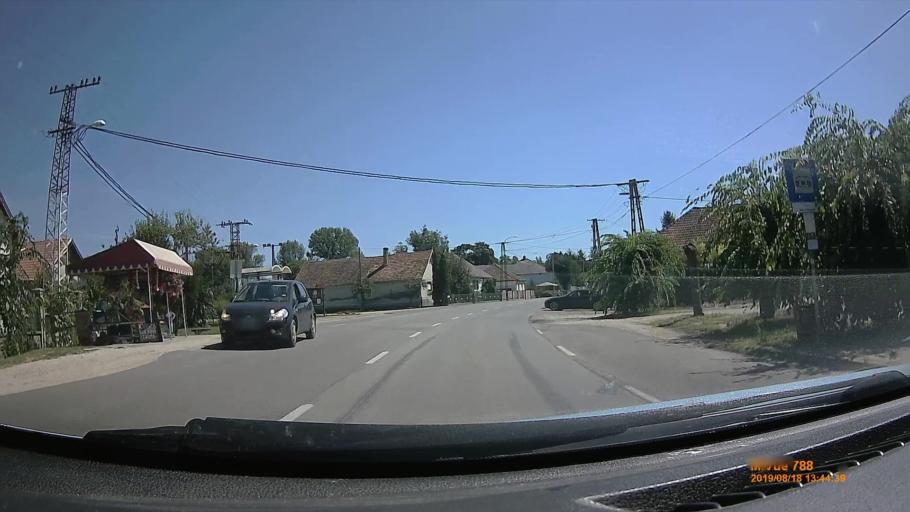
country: HU
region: Fejer
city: Cece
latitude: 46.7634
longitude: 18.6350
